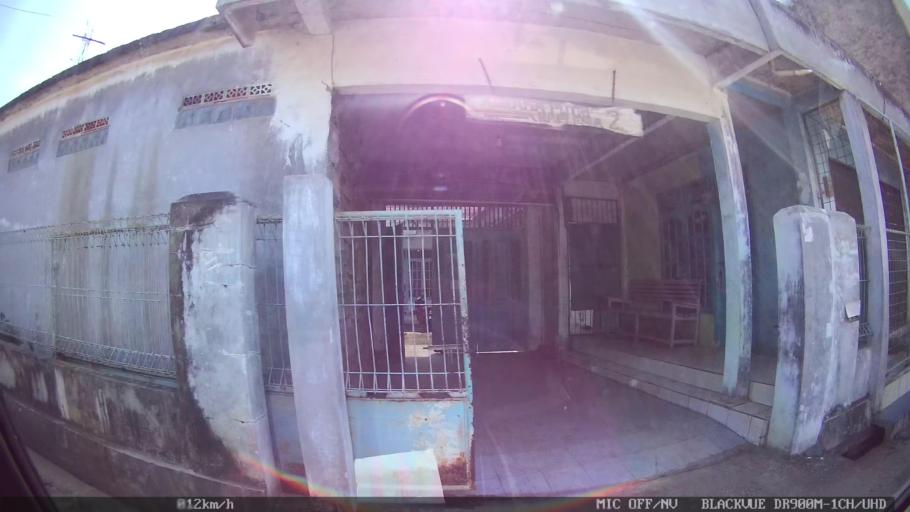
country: ID
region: Lampung
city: Kedaton
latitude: -5.3641
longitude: 105.2487
